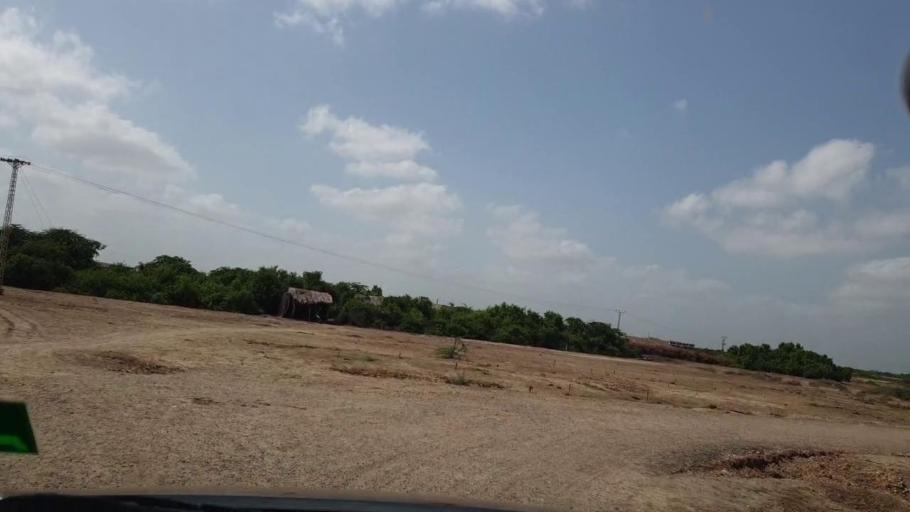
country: PK
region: Sindh
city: Kadhan
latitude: 24.5874
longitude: 69.1593
